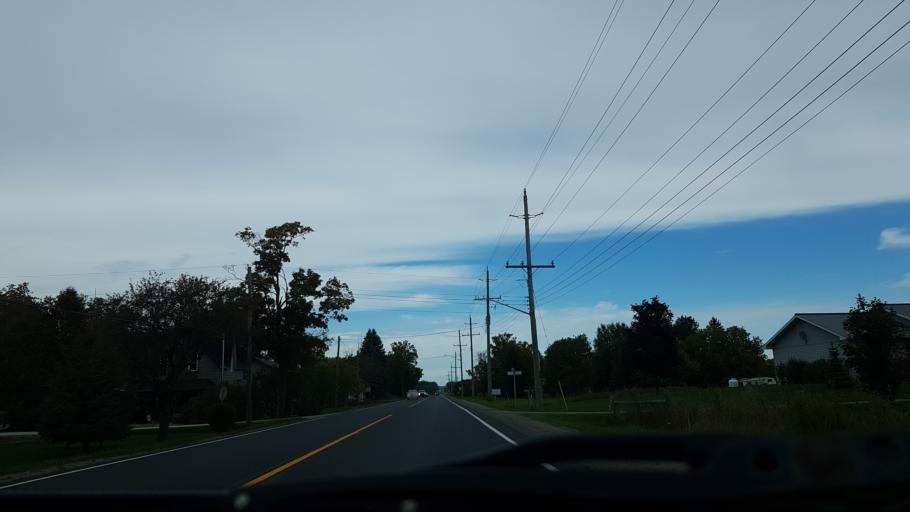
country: CA
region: Ontario
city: Angus
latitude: 44.3120
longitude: -80.0727
